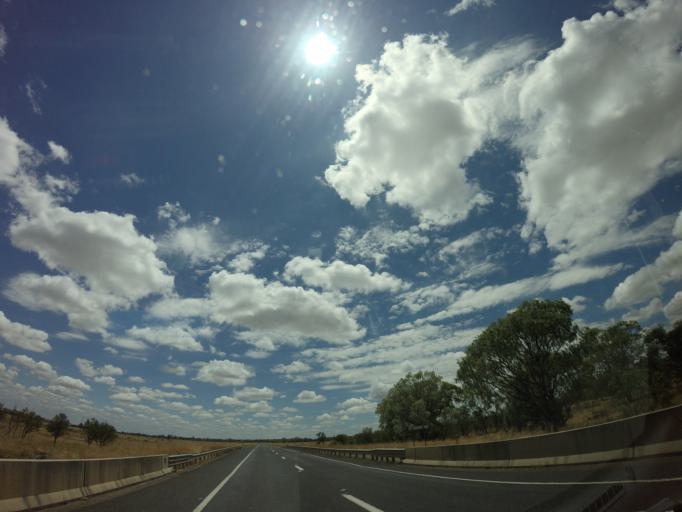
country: AU
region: New South Wales
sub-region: Moree Plains
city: Boggabilla
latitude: -28.9311
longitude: 150.1138
